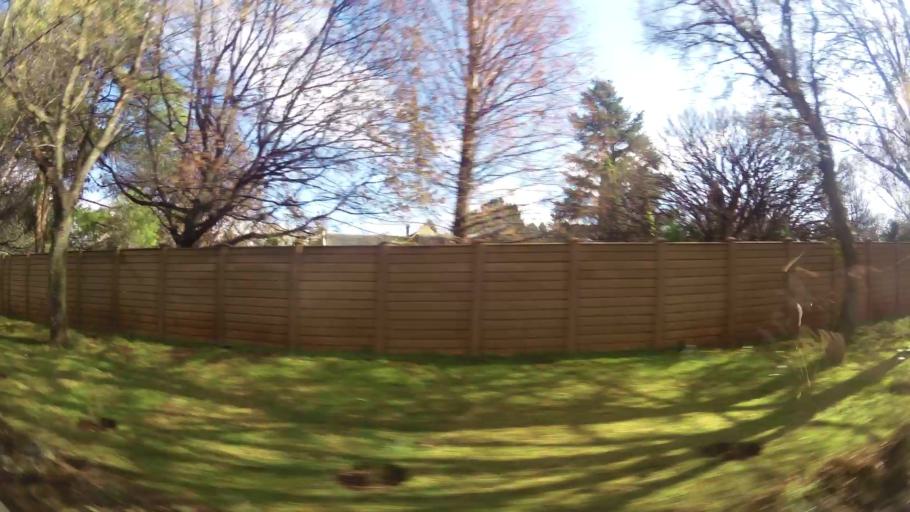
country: ZA
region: Gauteng
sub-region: Sedibeng District Municipality
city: Meyerton
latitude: -26.5464
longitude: 28.0650
